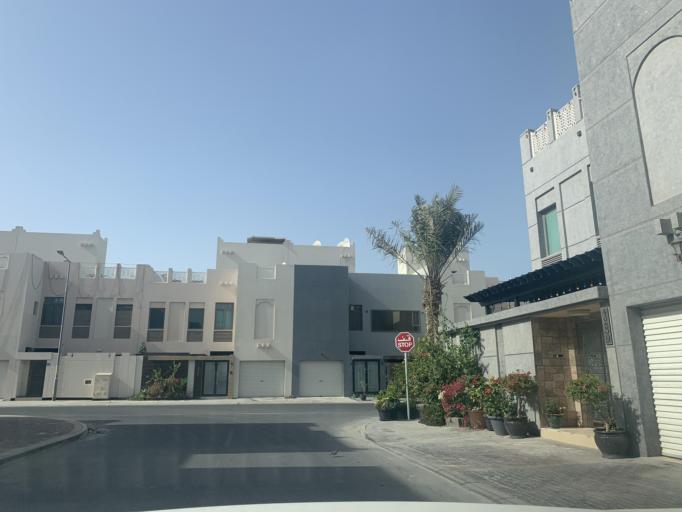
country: BH
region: Northern
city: Sitrah
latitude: 26.1600
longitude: 50.6276
